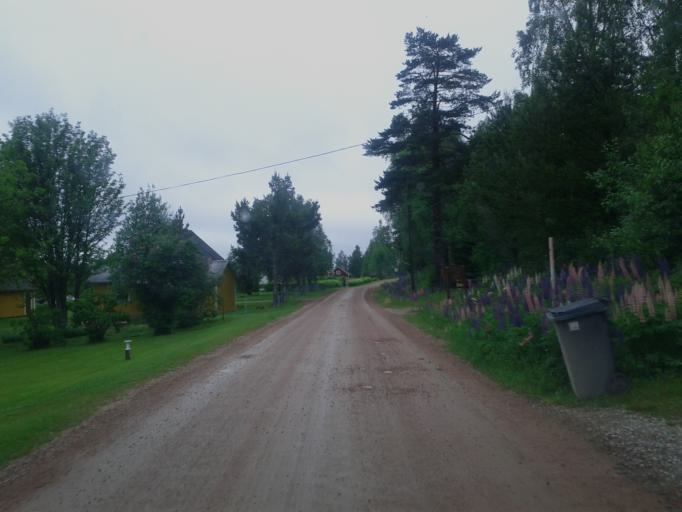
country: SE
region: Gaevleborg
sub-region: Hudiksvalls Kommun
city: Delsbo
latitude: 62.1825
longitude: 16.4770
